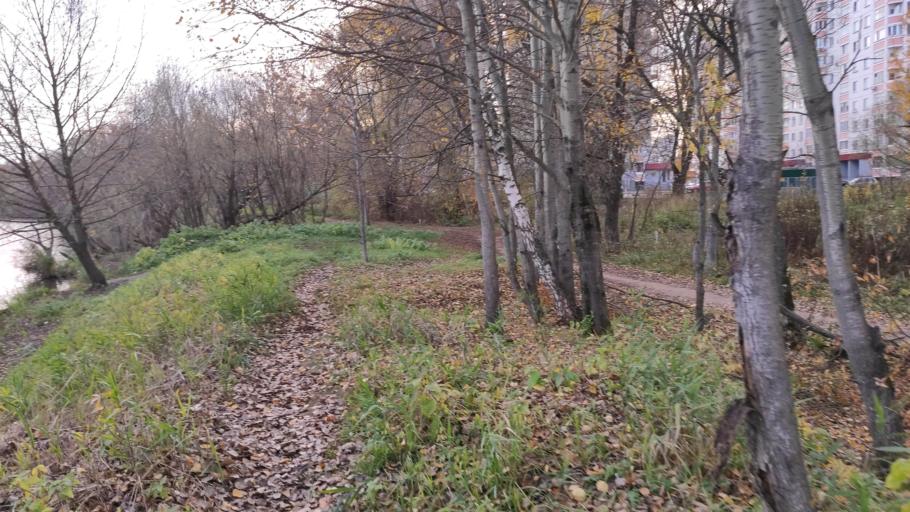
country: RU
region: Moskovskaya
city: Noginsk
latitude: 55.8680
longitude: 38.4513
